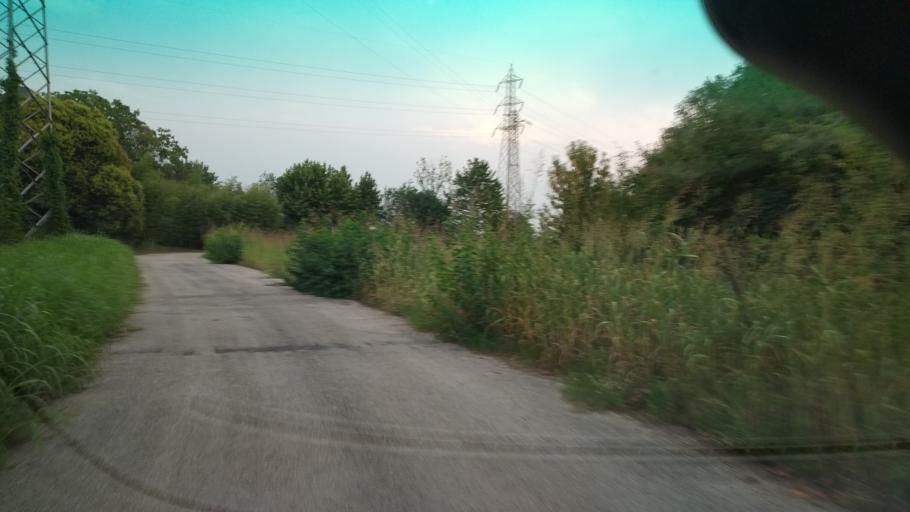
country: IT
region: Veneto
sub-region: Provincia di Vicenza
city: Montecchio Precalcino
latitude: 45.6813
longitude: 11.5612
